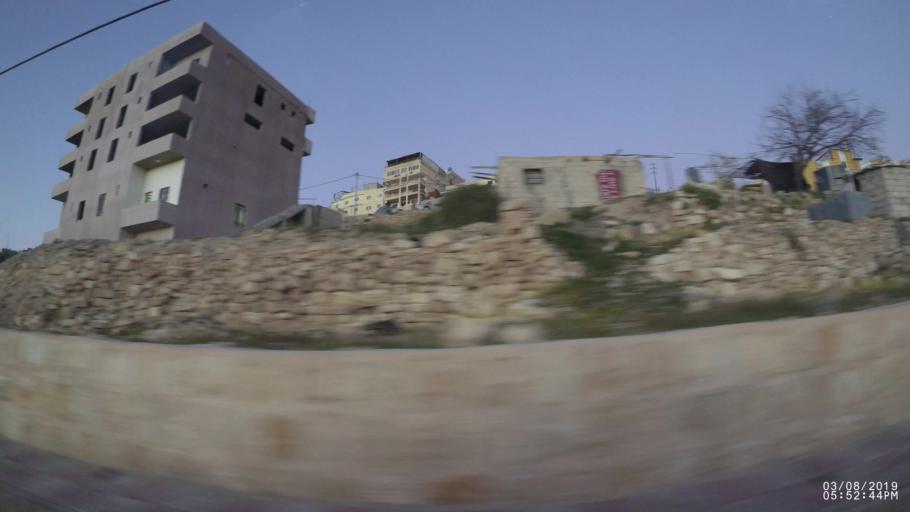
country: JO
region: Ma'an
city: Petra
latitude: 30.3211
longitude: 35.4820
